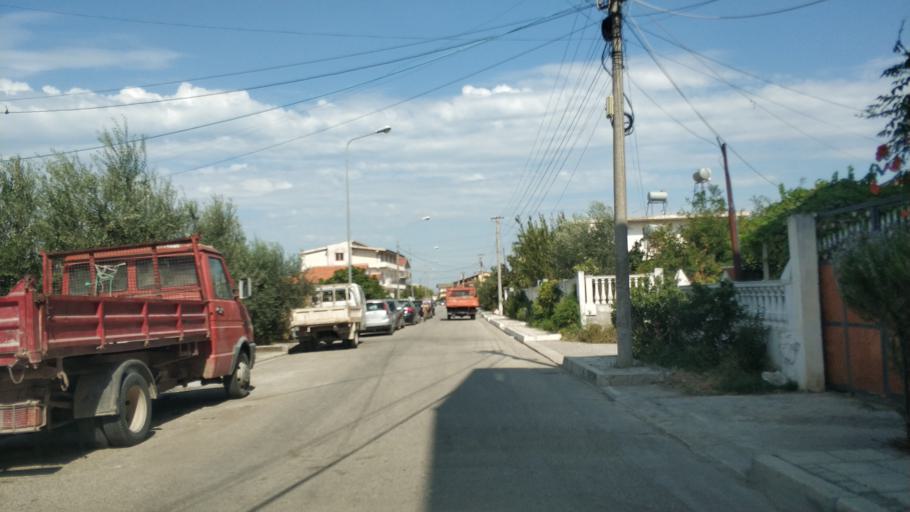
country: AL
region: Fier
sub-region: Rrethi i Lushnjes
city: Divjake
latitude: 40.9957
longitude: 19.5286
